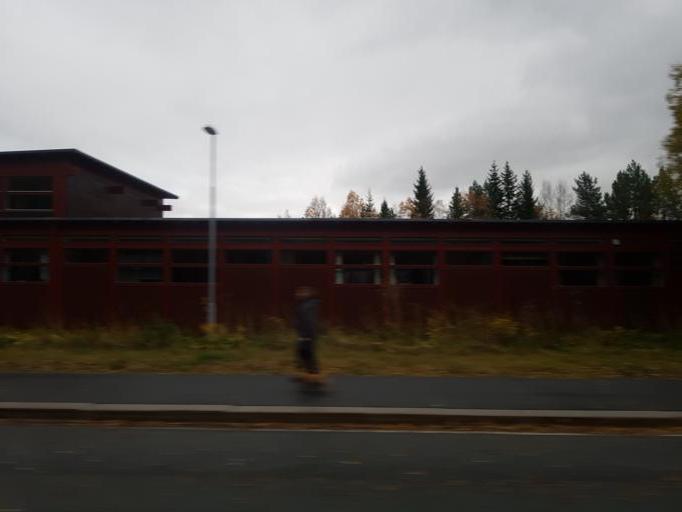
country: NO
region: Sor-Trondelag
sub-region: Trondheim
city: Trondheim
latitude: 63.3752
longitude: 10.3367
